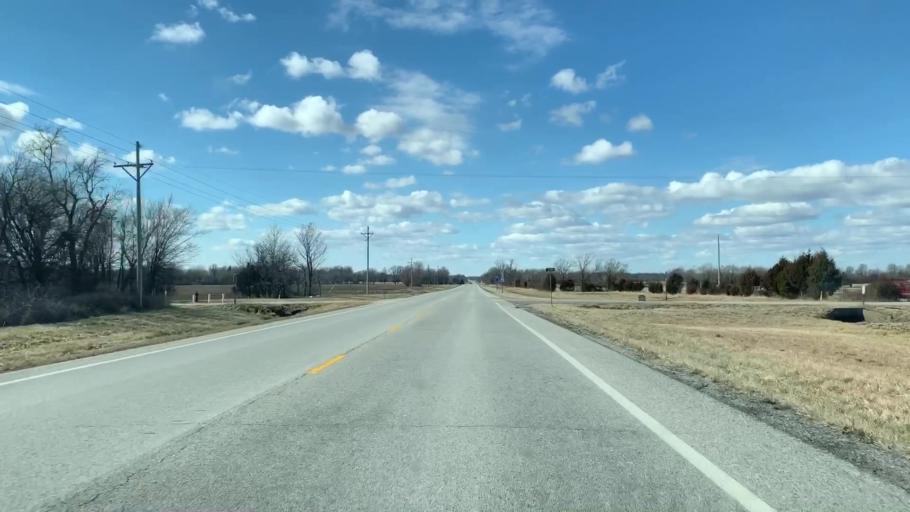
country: US
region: Kansas
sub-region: Cherokee County
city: Columbus
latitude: 37.1782
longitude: -94.7951
